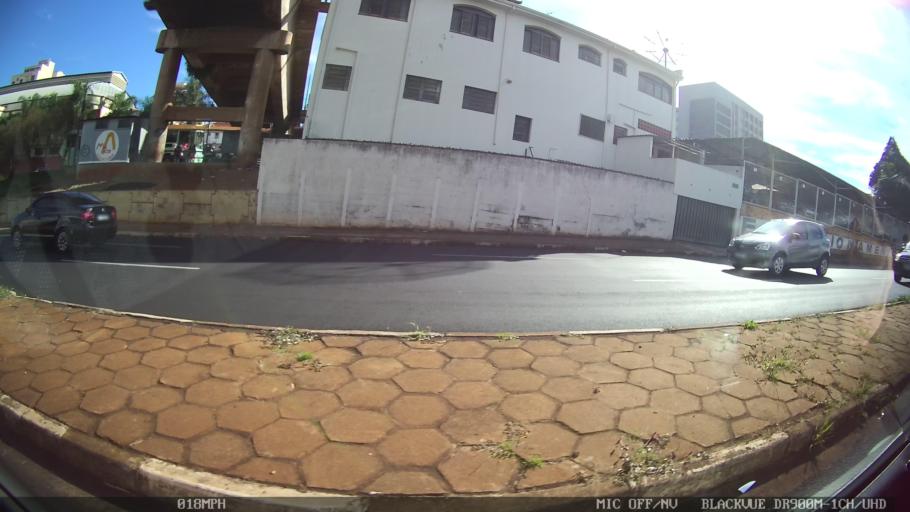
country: BR
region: Sao Paulo
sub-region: Araraquara
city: Araraquara
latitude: -21.7917
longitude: -48.1724
